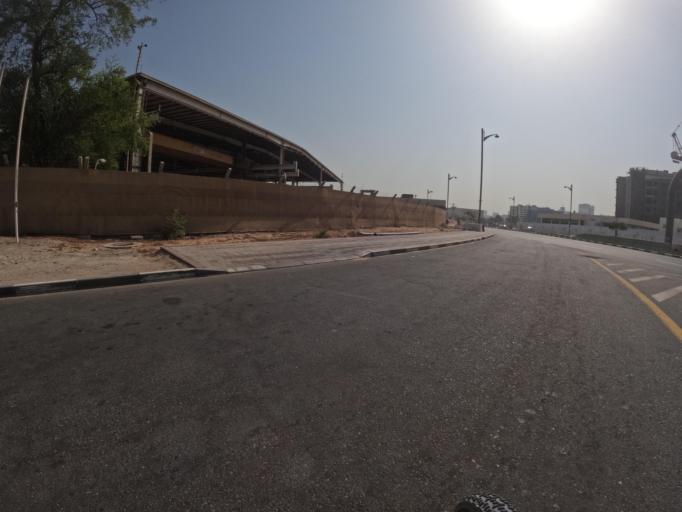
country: AE
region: Ash Shariqah
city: Sharjah
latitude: 25.2503
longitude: 55.2769
